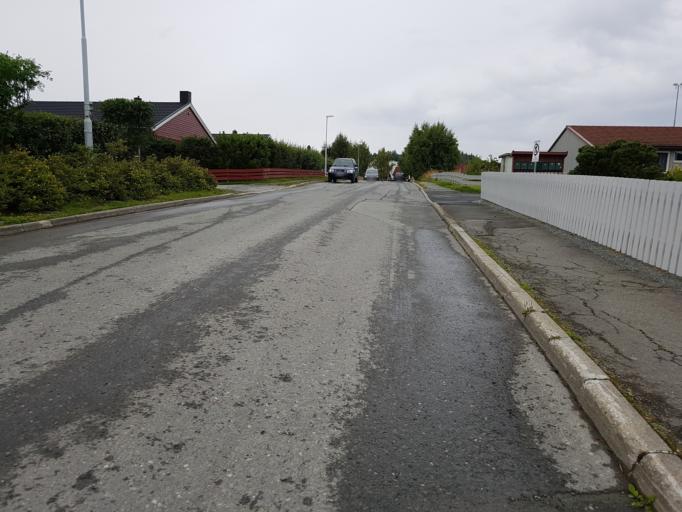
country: NO
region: Sor-Trondelag
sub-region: Trondheim
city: Trondheim
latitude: 63.3911
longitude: 10.3641
